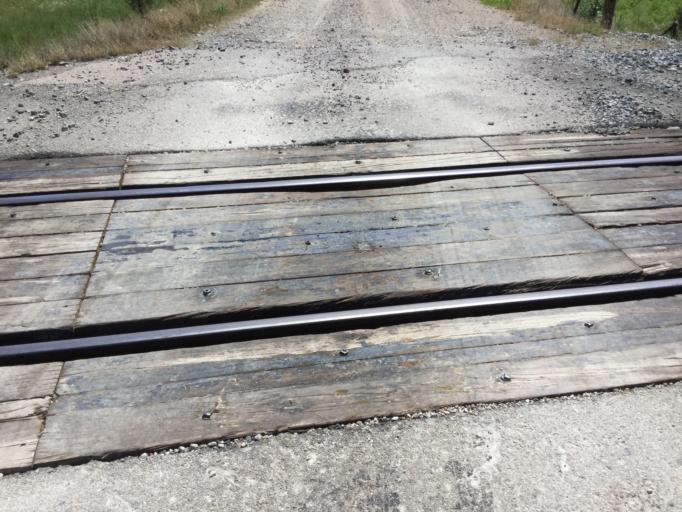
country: US
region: Kansas
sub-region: Woodson County
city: Yates Center
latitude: 37.8209
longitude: -95.6907
